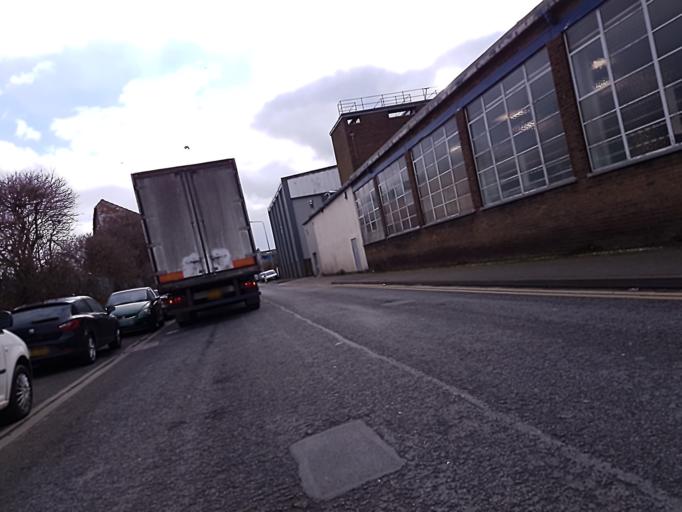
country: GB
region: England
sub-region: North East Lincolnshire
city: Grimsby
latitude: 53.5758
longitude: -0.0702
